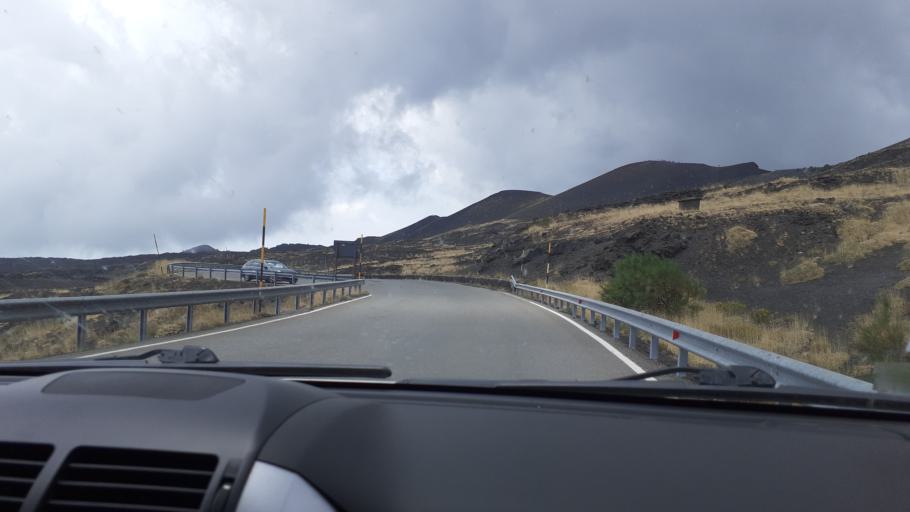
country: IT
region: Sicily
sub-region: Catania
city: Nicolosi
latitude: 37.7006
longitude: 15.0132
